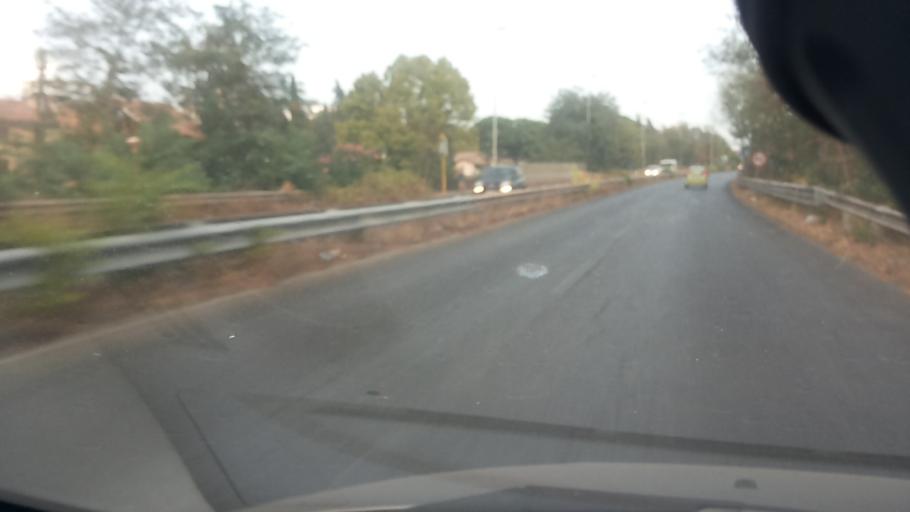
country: IT
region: Latium
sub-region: Citta metropolitana di Roma Capitale
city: Frascati
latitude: 41.8221
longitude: 12.6410
